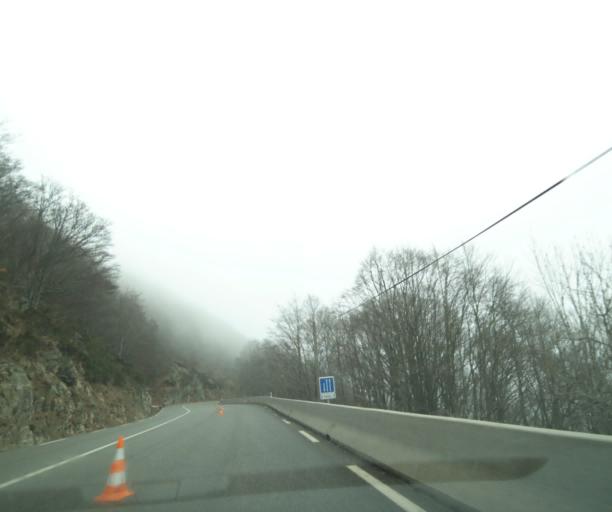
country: FR
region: Languedoc-Roussillon
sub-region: Departement de la Lozere
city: Langogne
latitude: 44.6916
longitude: 4.0356
